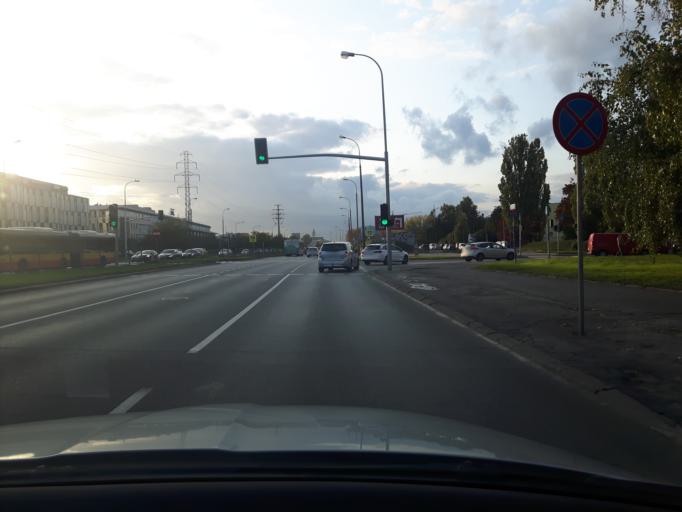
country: PL
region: Masovian Voivodeship
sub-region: Warszawa
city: Ursynow
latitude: 52.1511
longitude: 21.0277
